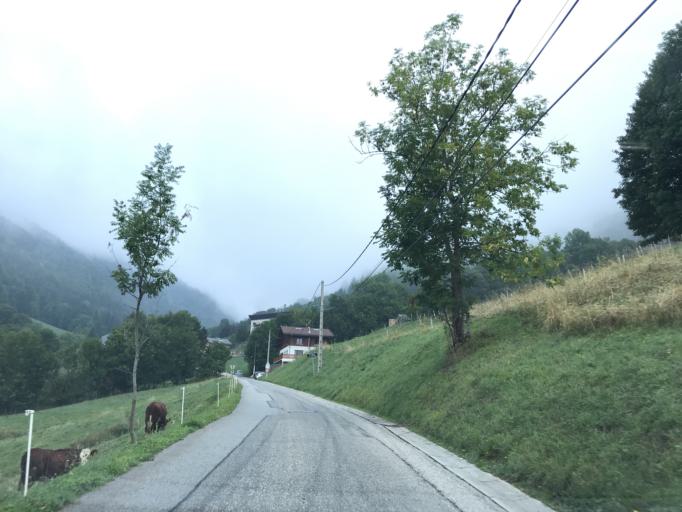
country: FR
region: Rhone-Alpes
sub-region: Departement de la Haute-Savoie
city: Doussard
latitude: 45.8091
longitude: 6.2620
